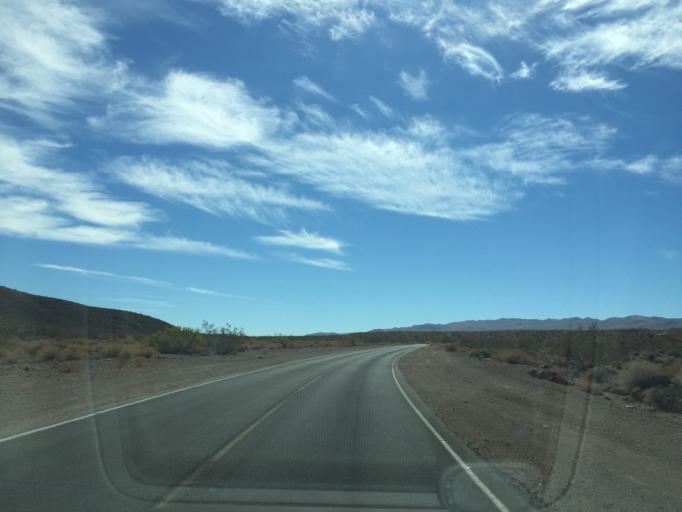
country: US
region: Nevada
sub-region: Nye County
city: Beatty
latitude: 36.2792
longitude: -116.6684
